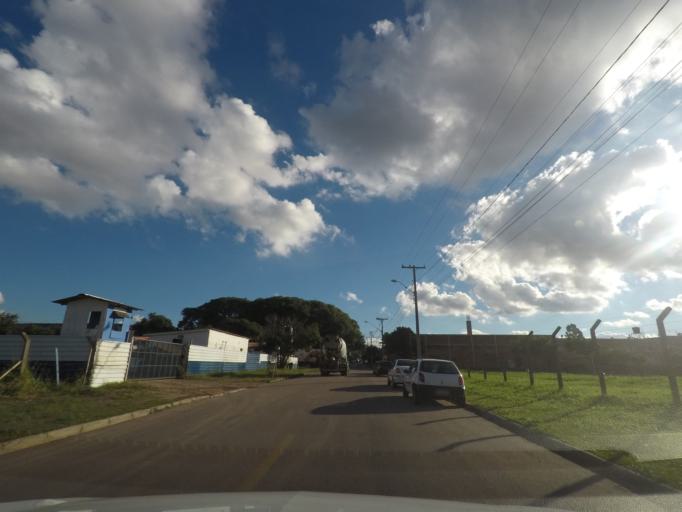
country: BR
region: Parana
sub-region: Curitiba
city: Curitiba
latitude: -25.4851
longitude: -49.2643
